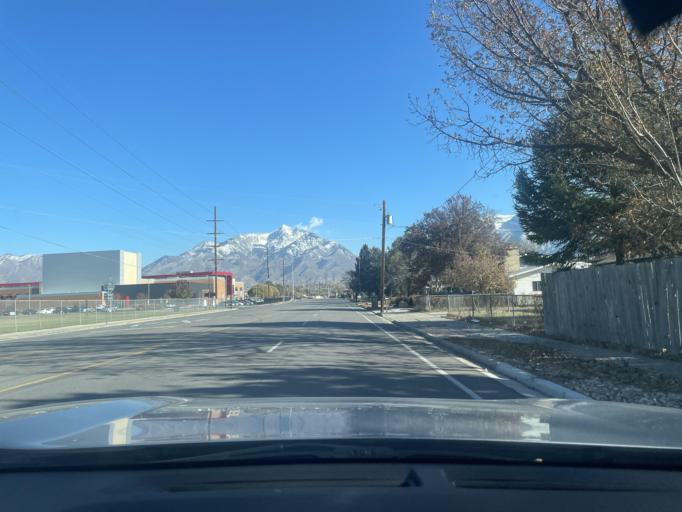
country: US
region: Utah
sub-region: Salt Lake County
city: Sandy City
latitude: 40.5805
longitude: -111.8855
